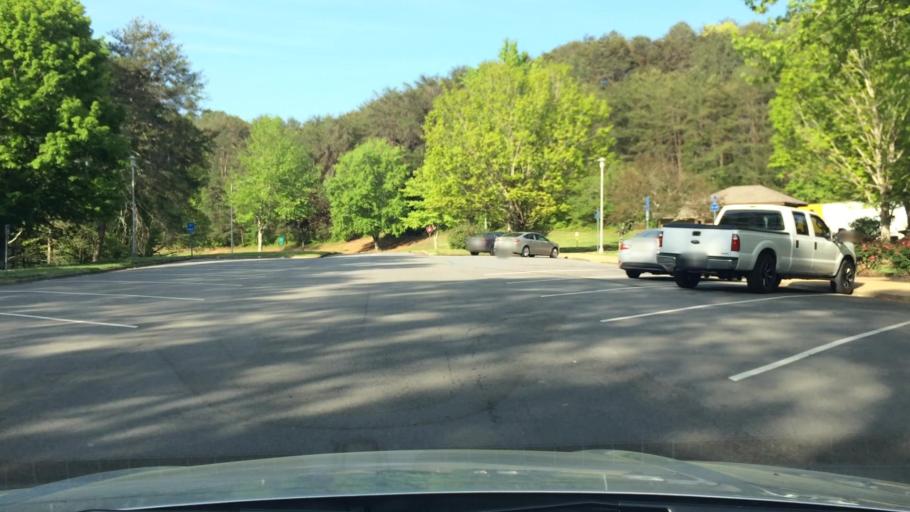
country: US
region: Georgia
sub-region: Dade County
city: Trenton
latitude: 34.7076
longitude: -85.5601
